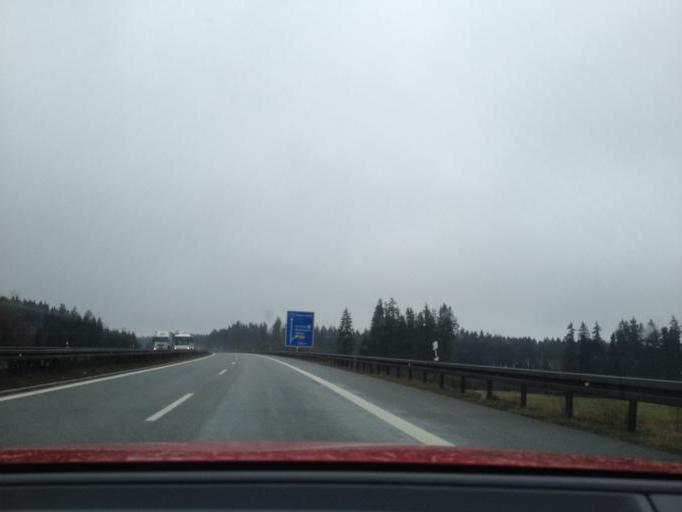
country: DE
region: Bavaria
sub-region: Upper Franconia
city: Rehau
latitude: 50.2755
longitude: 12.0240
